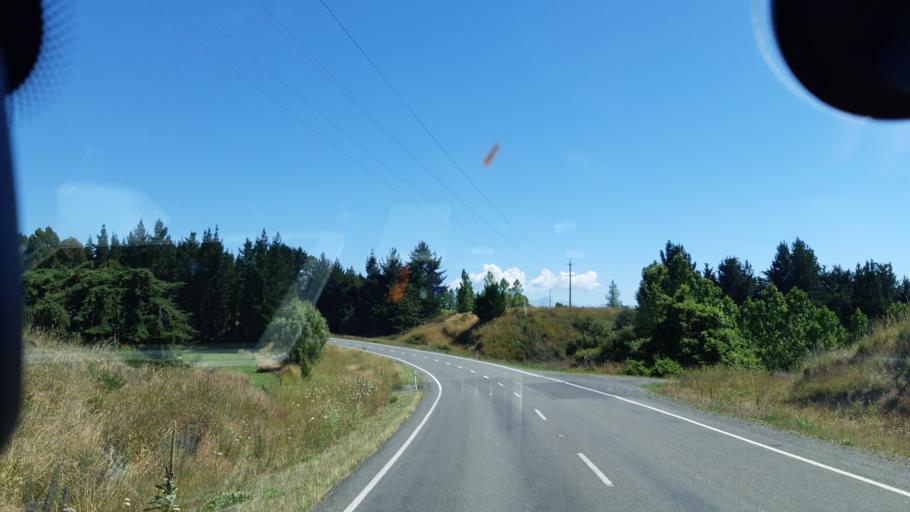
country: NZ
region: Canterbury
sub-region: Kaikoura District
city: Kaikoura
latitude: -42.7530
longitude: 173.2730
